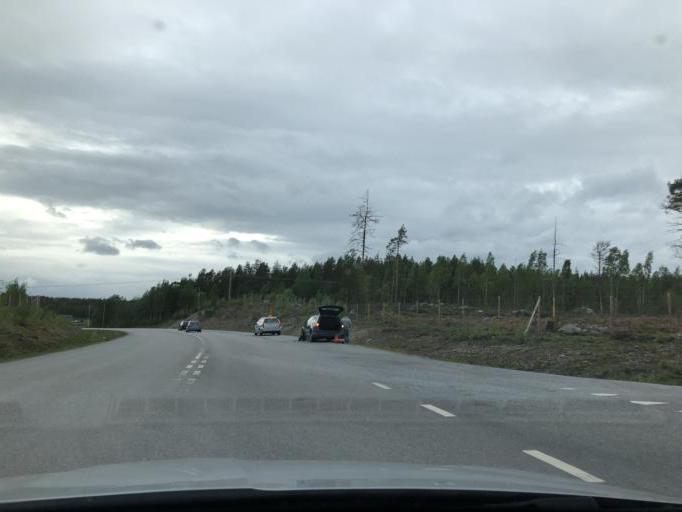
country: SE
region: Norrbotten
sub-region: Pitea Kommun
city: Norrfjarden
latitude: 65.3727
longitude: 21.4264
